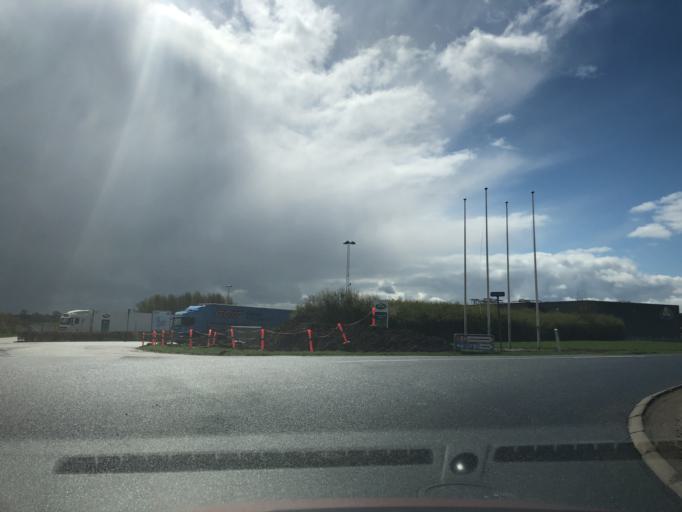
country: DK
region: South Denmark
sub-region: Kolding Kommune
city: Christiansfeld
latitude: 55.3565
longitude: 9.4957
